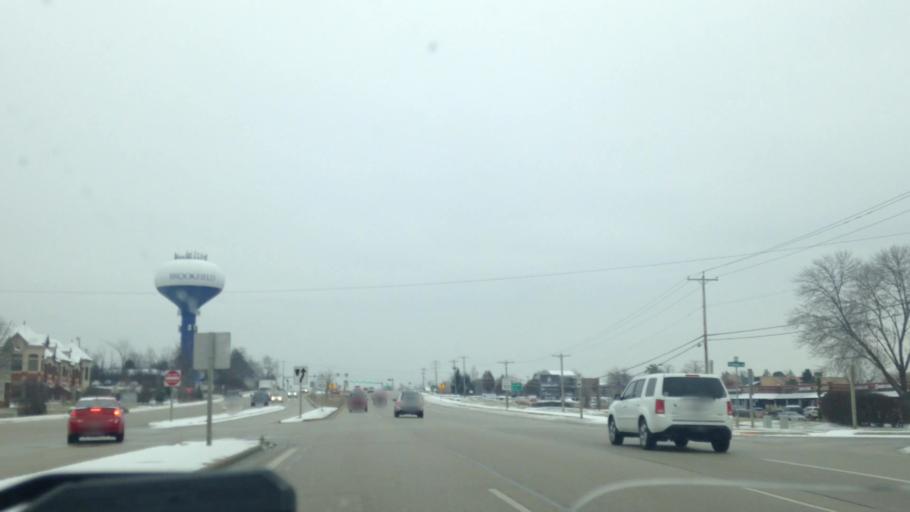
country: US
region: Wisconsin
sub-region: Waukesha County
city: Brookfield
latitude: 43.0902
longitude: -88.1313
